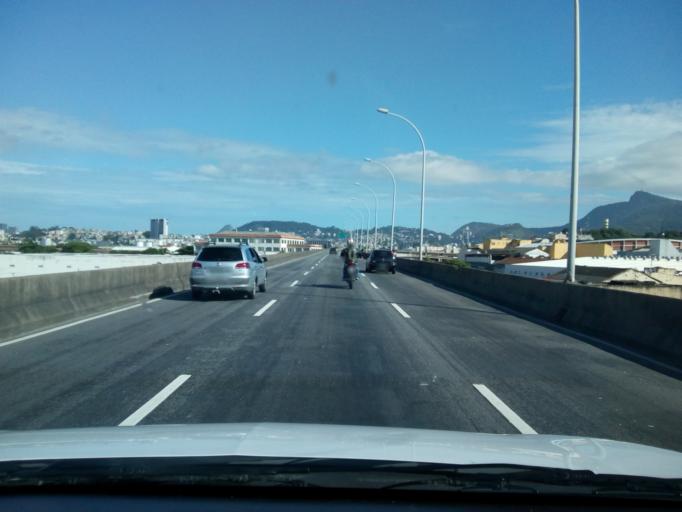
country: BR
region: Rio de Janeiro
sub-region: Rio De Janeiro
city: Rio de Janeiro
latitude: -22.8925
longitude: -43.2214
